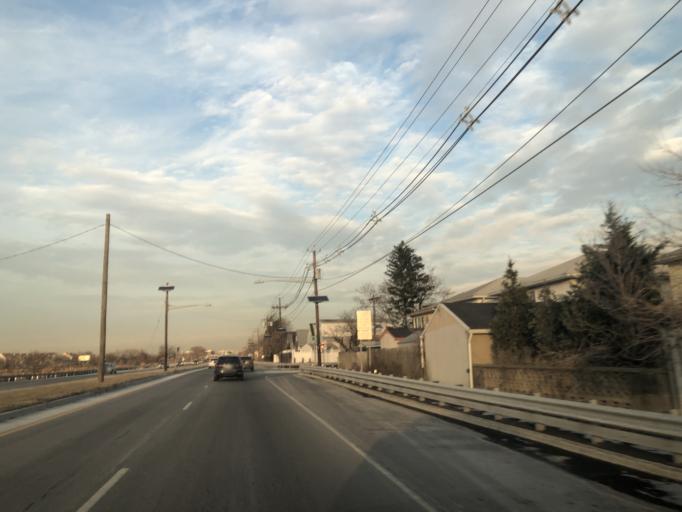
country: US
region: New Jersey
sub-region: Hudson County
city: Bayonne
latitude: 40.6990
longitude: -74.1045
